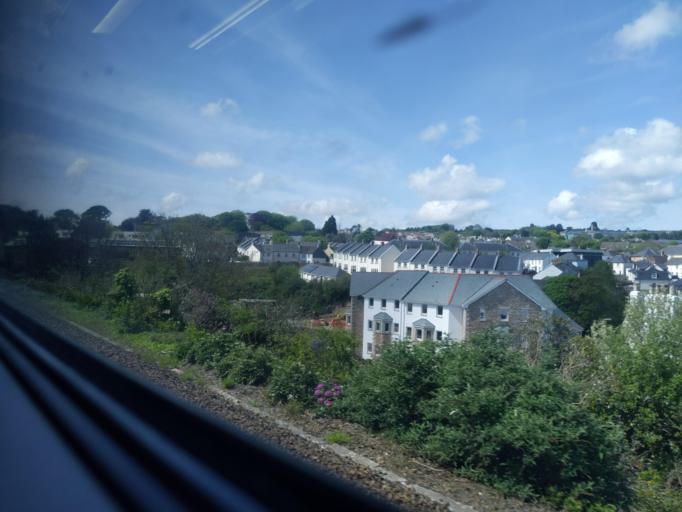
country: GB
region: England
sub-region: Cornwall
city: St Austell
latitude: 50.3389
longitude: -4.7778
